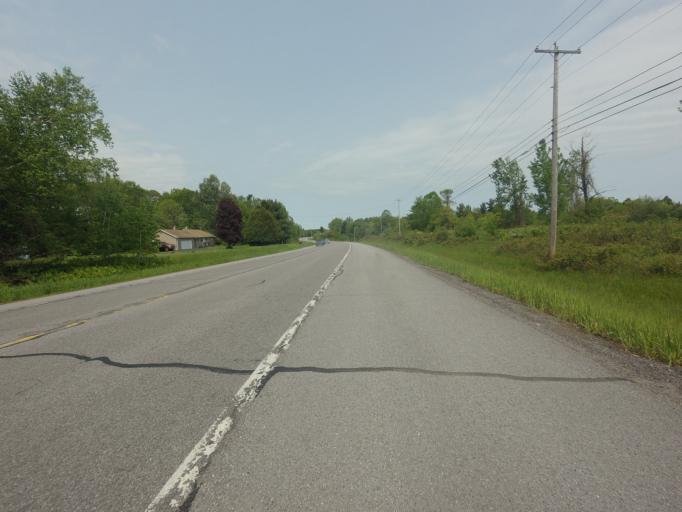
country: US
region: New York
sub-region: Jefferson County
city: Brownville
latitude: 44.0083
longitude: -76.0130
